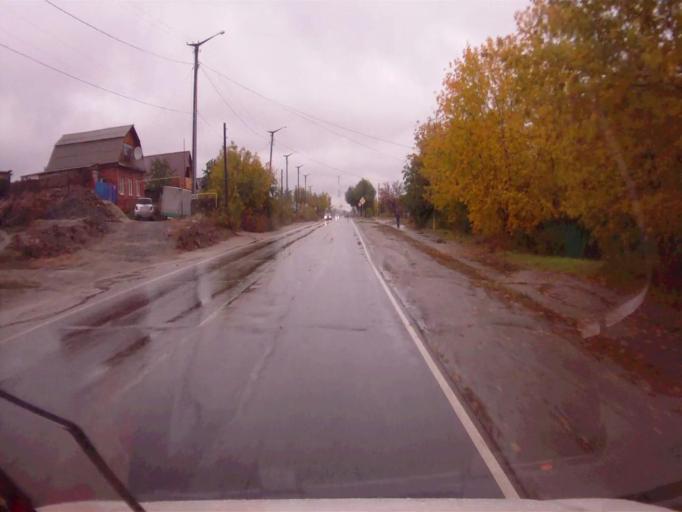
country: RU
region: Chelyabinsk
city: Kyshtym
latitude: 55.7113
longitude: 60.5576
